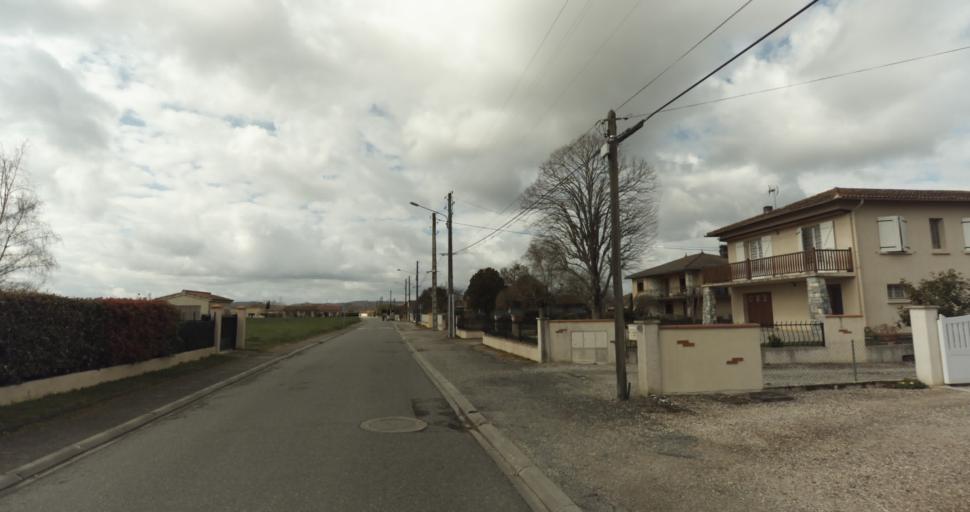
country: FR
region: Midi-Pyrenees
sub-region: Departement de la Haute-Garonne
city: Auterive
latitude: 43.3484
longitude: 1.4646
